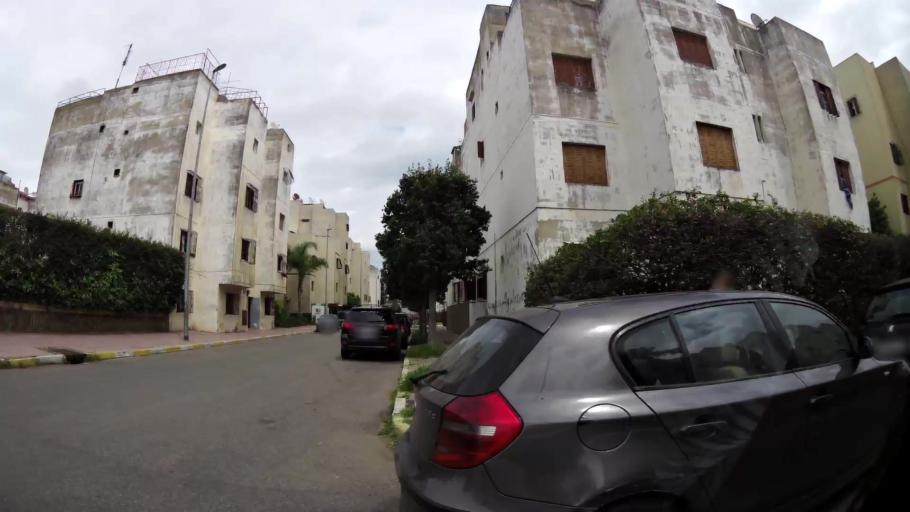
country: MA
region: Grand Casablanca
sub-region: Casablanca
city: Casablanca
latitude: 33.5787
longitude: -7.5613
